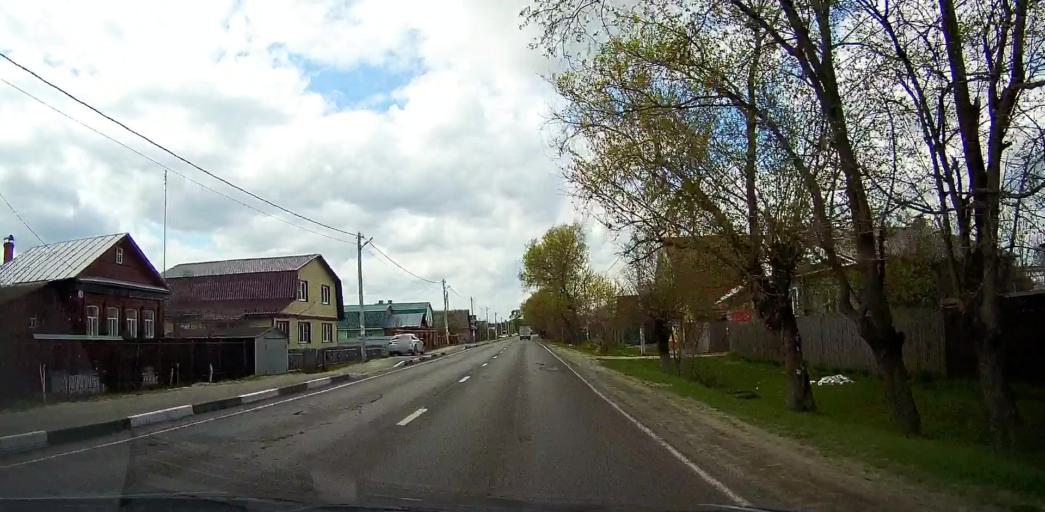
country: RU
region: Moskovskaya
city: Davydovo
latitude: 55.6389
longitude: 38.8645
